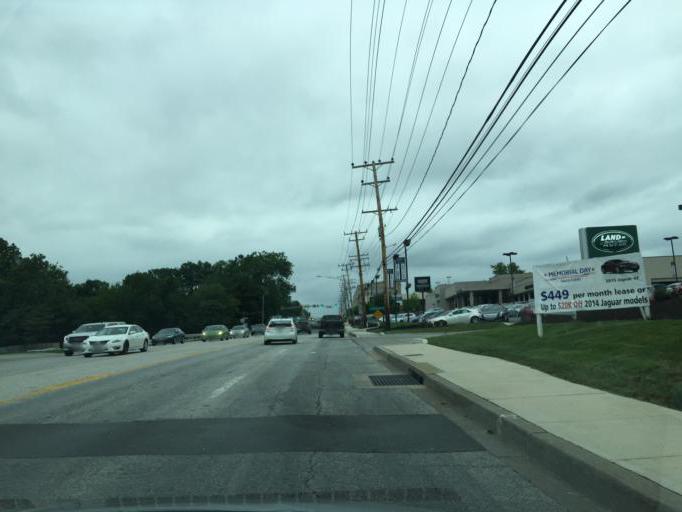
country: US
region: Maryland
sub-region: Baltimore County
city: Cockeysville
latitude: 39.4711
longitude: -76.6395
